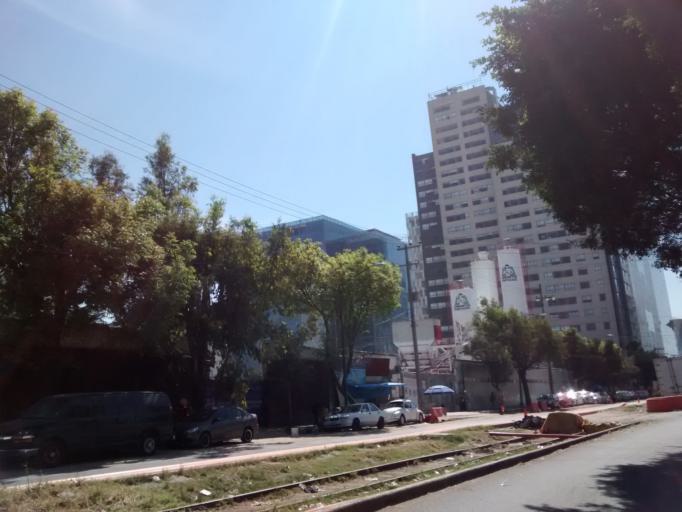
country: MX
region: Mexico City
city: Miguel Hidalgo
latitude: 19.4451
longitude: -99.2049
